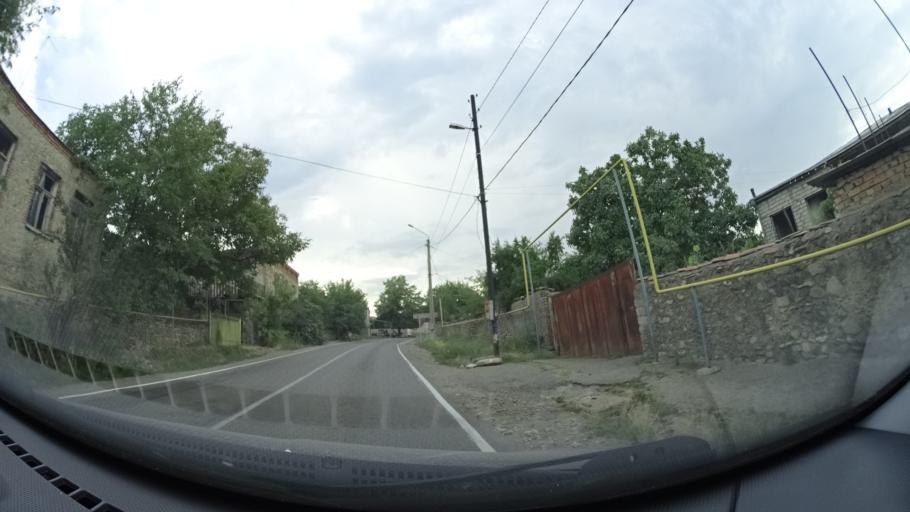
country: GE
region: Kakheti
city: Tsinandali
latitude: 41.8324
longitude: 45.6732
